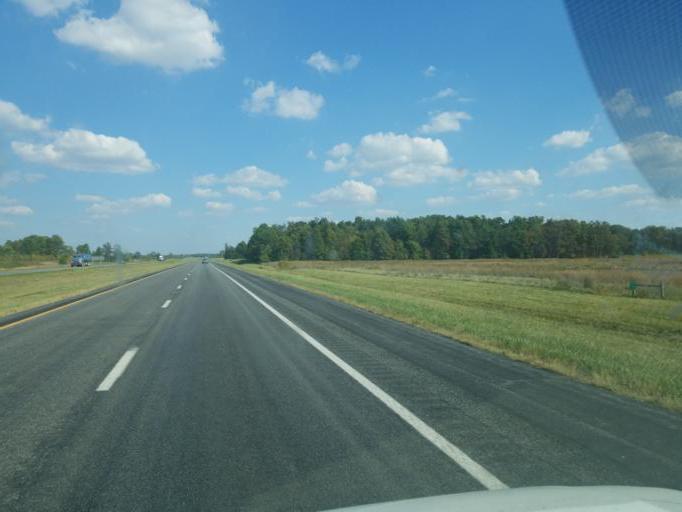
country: US
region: Ohio
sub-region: Hancock County
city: Arlington
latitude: 40.8287
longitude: -83.5931
